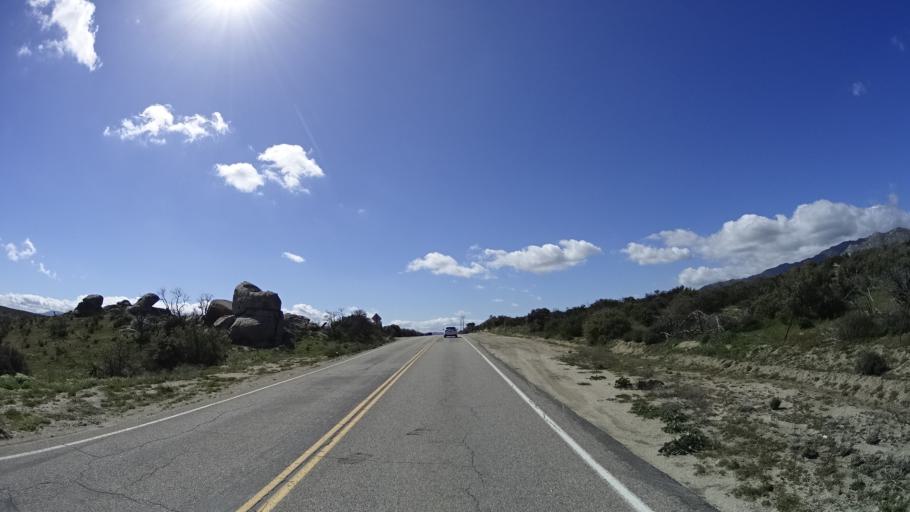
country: US
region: California
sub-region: San Diego County
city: Borrego Springs
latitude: 33.2105
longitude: -116.4960
